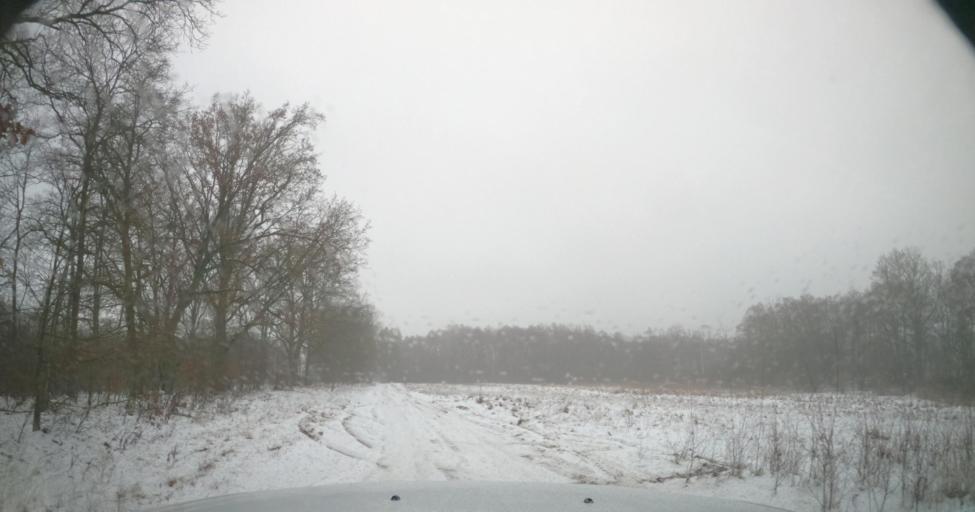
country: PL
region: West Pomeranian Voivodeship
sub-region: Powiat kamienski
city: Golczewo
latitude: 53.7733
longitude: 14.9544
